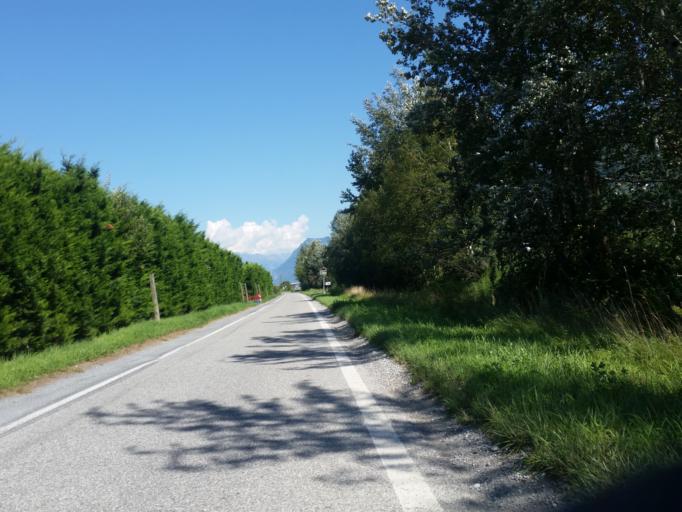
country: CH
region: Valais
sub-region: Conthey District
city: Conthey
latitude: 46.2156
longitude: 7.3251
